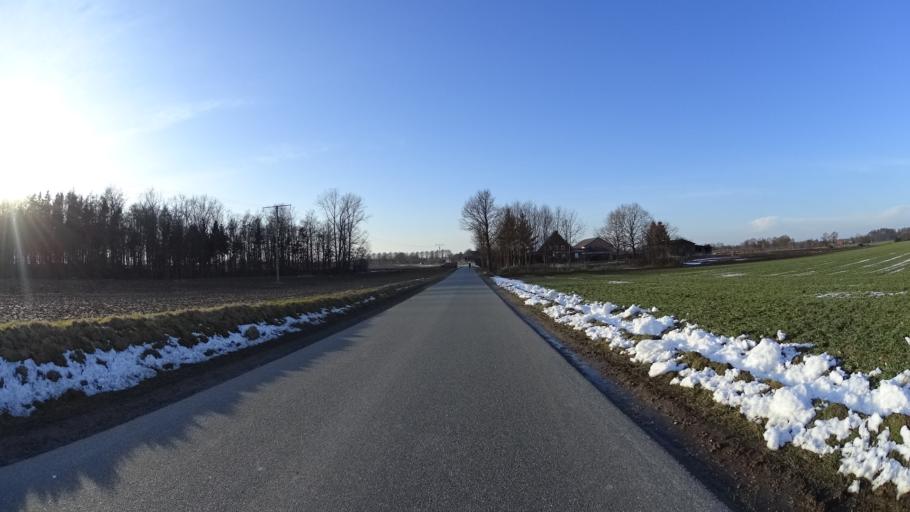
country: DE
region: Schleswig-Holstein
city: Fargau-Pratjau
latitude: 54.3379
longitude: 10.4098
